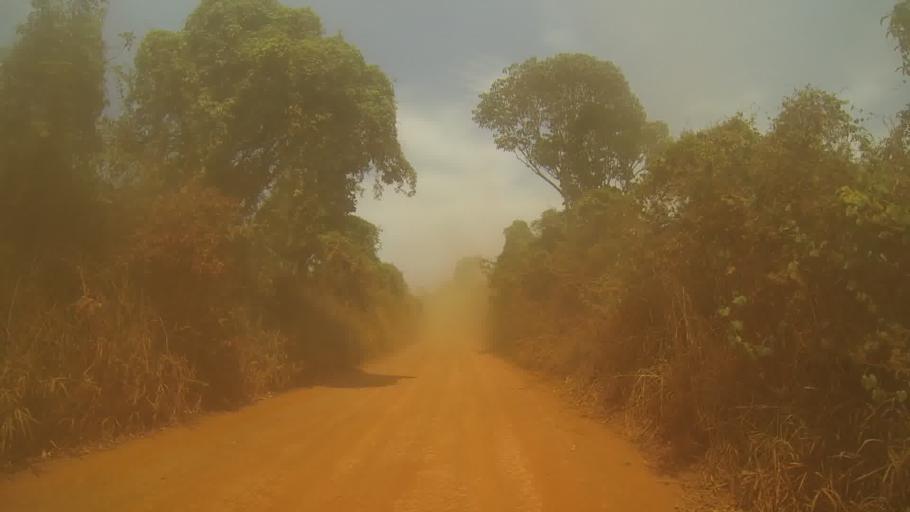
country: BR
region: Minas Gerais
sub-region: Bambui
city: Bambui
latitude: -20.0057
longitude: -45.9311
